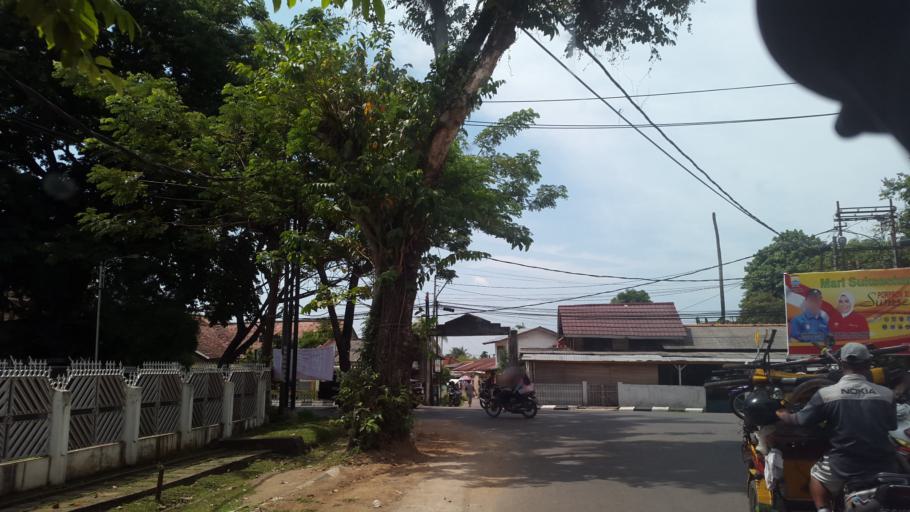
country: ID
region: South Sumatra
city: Plaju
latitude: -2.9956
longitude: 104.7482
